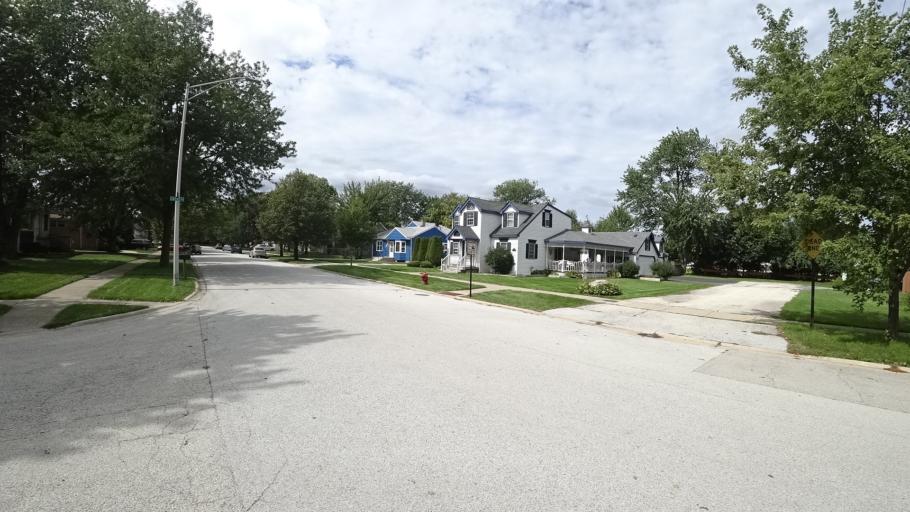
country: US
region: Illinois
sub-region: Cook County
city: Burbank
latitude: 41.7184
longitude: -87.7940
